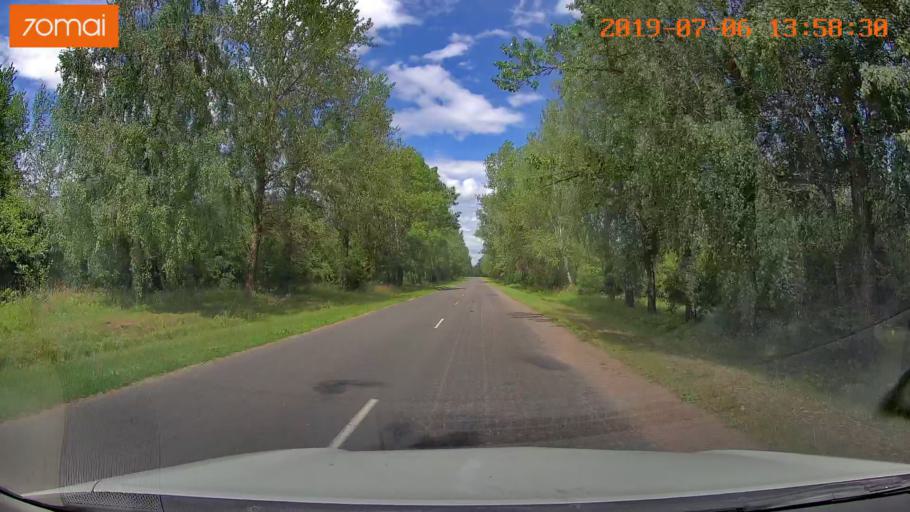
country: BY
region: Minsk
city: Ivyanyets
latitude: 53.7848
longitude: 26.8093
